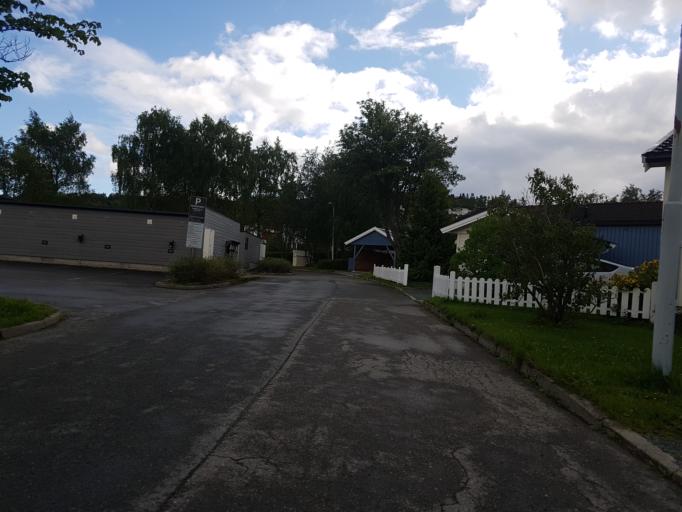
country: NO
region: Sor-Trondelag
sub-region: Trondheim
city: Trondheim
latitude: 63.4122
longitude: 10.4539
